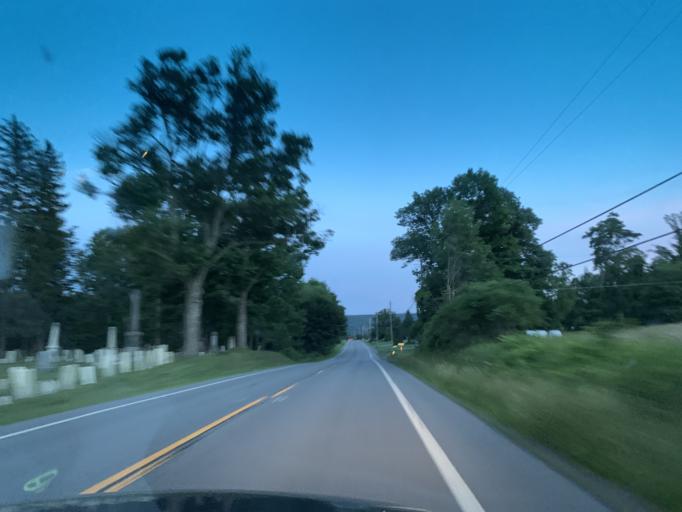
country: US
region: New York
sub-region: Chenango County
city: New Berlin
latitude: 42.5939
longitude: -75.3377
